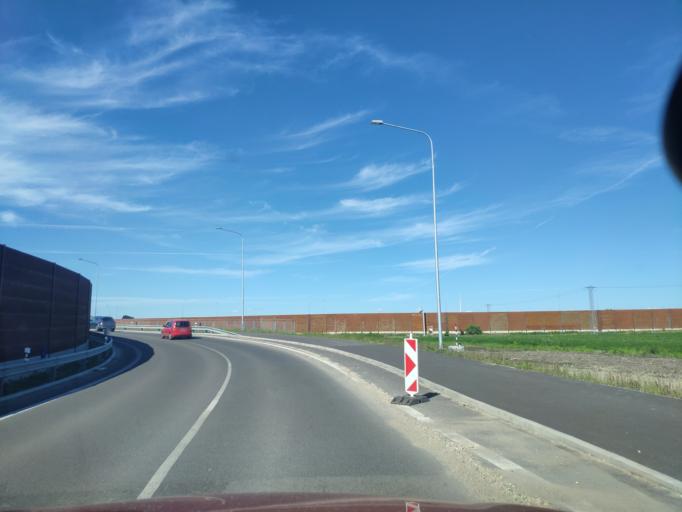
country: SK
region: Bratislavsky
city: Svaty Jur
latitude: 48.2097
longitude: 17.2208
